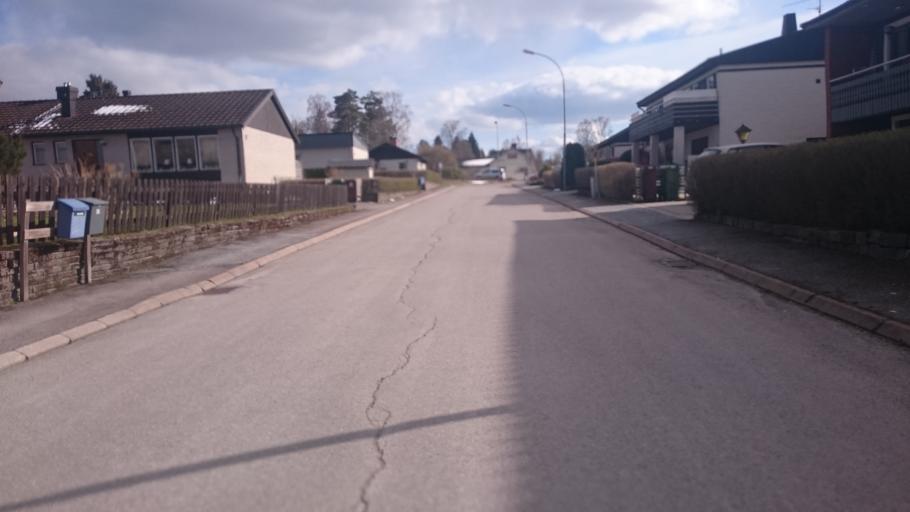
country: SE
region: OErebro
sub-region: Karlskoga Kommun
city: Karlskoga
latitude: 59.3104
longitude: 14.4905
